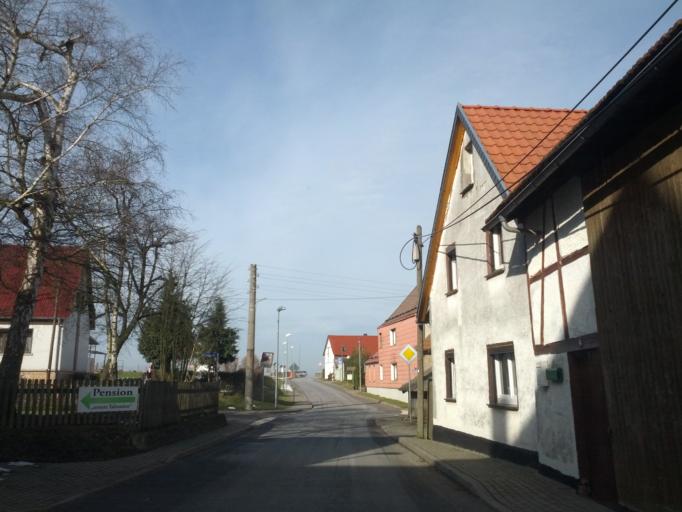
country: DE
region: Thuringia
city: Weberstedt
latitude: 51.0647
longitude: 10.4919
